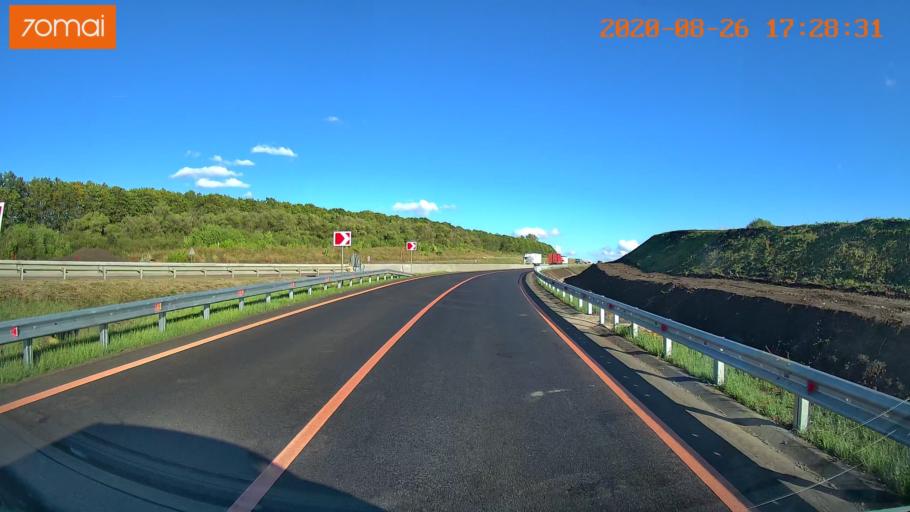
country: RU
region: Tula
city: Kazachka
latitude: 53.4623
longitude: 38.1362
